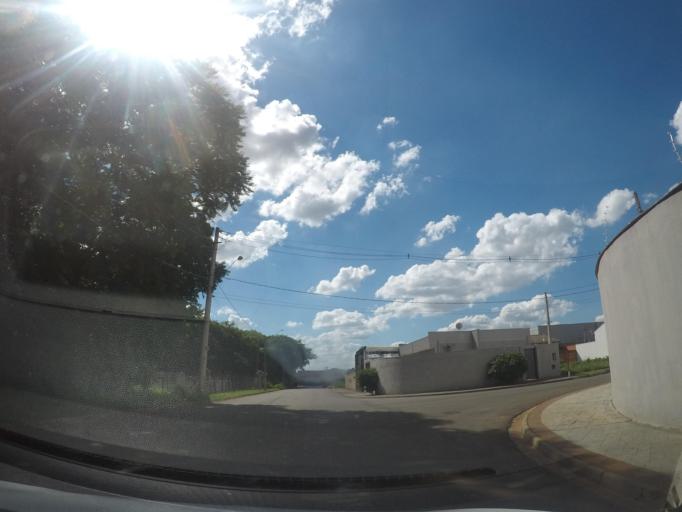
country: BR
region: Sao Paulo
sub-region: Sumare
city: Sumare
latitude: -22.8372
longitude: -47.2735
